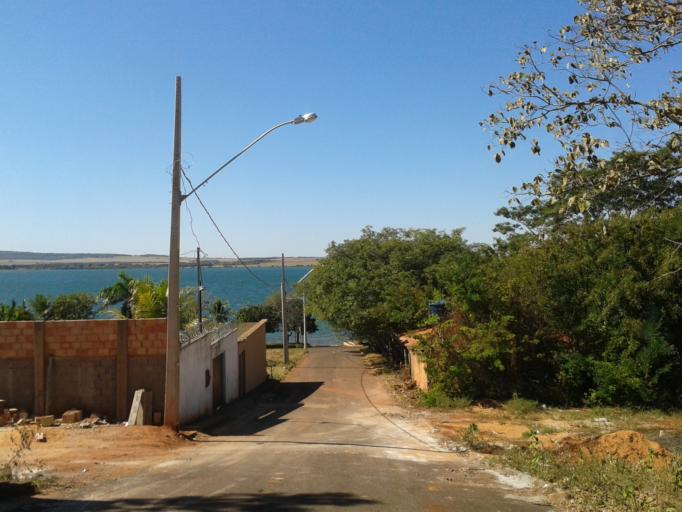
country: BR
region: Minas Gerais
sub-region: Capinopolis
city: Capinopolis
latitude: -18.5171
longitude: -49.4986
